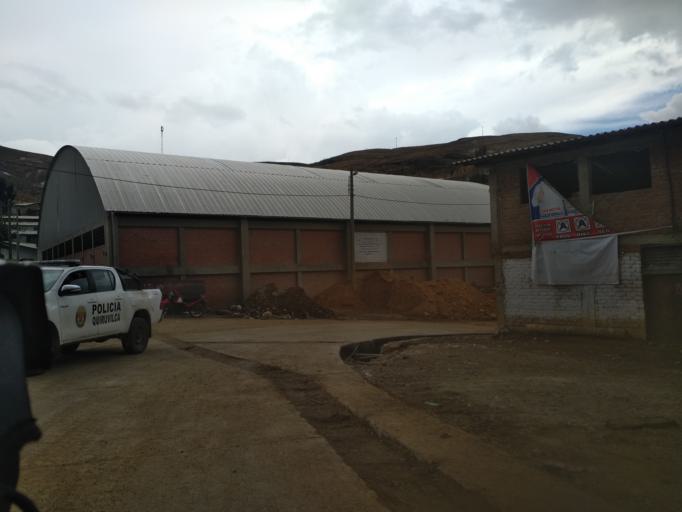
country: PE
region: La Libertad
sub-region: Provincia de Santiago de Chuco
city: Quiruvilca
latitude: -8.0002
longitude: -78.3071
